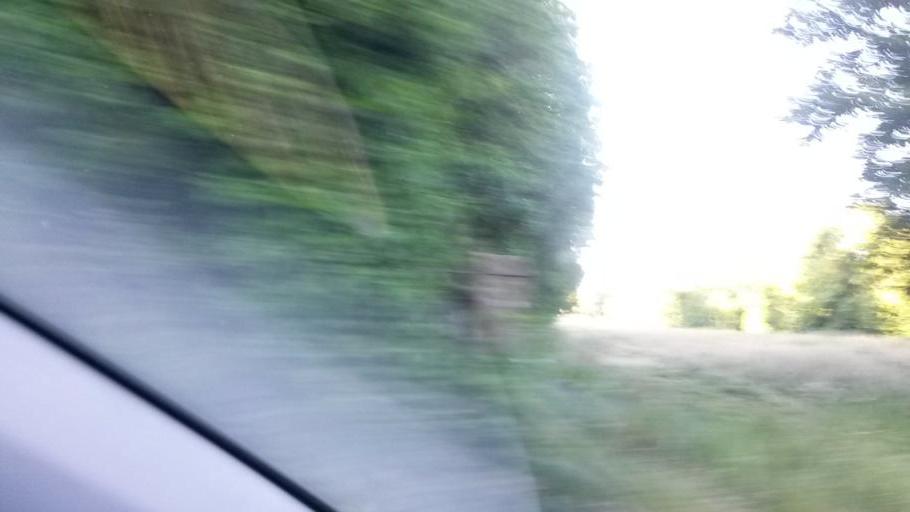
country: IE
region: Leinster
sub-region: An Mhi
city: Ashbourne
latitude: 53.5760
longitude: -6.3667
